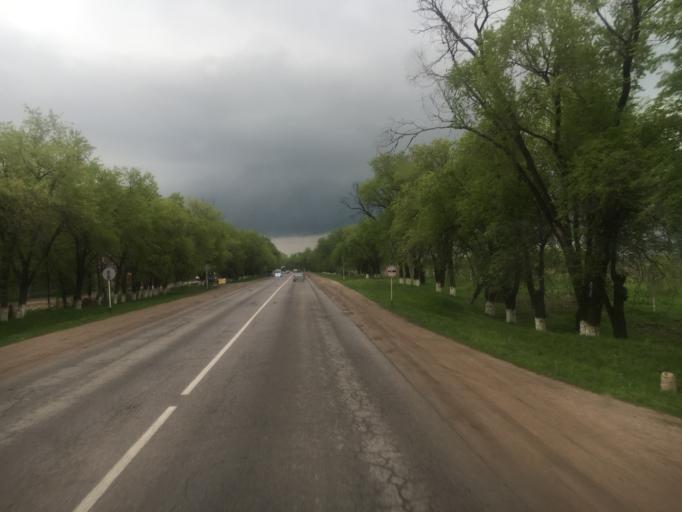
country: KZ
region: Almaty Oblysy
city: Burunday
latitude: 43.2380
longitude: 76.6655
